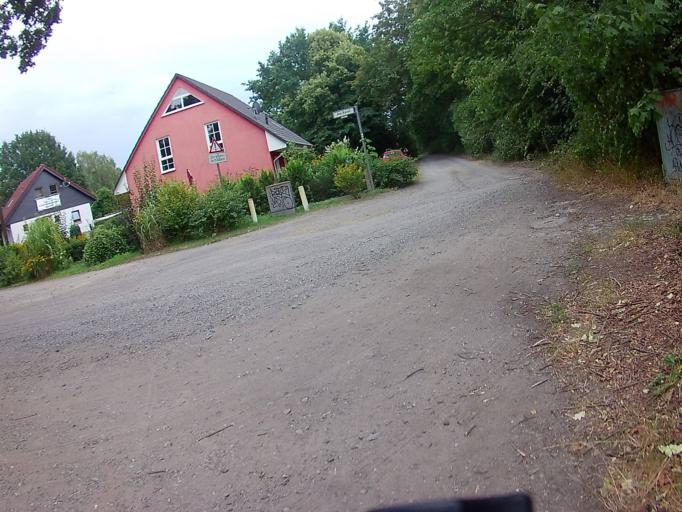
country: DE
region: Berlin
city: Adlershof
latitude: 52.4259
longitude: 13.5560
